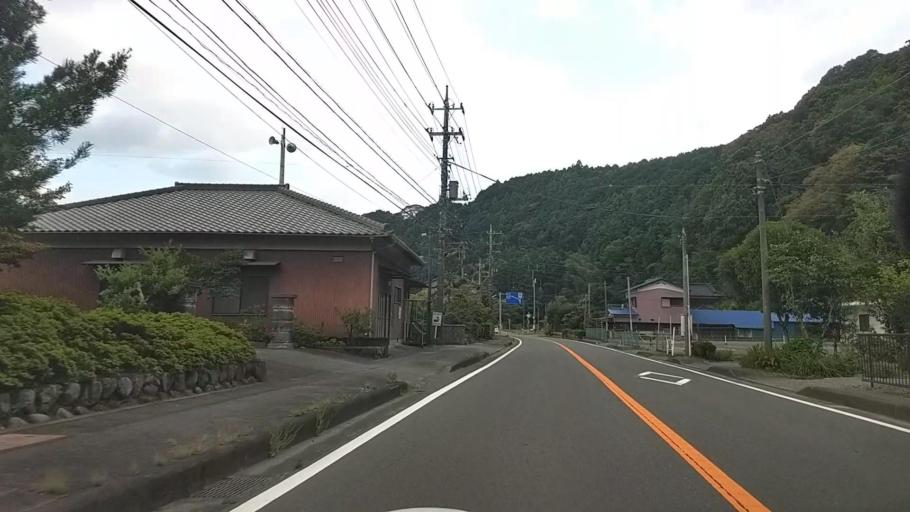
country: JP
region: Shizuoka
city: Fujinomiya
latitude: 35.2281
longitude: 138.5082
